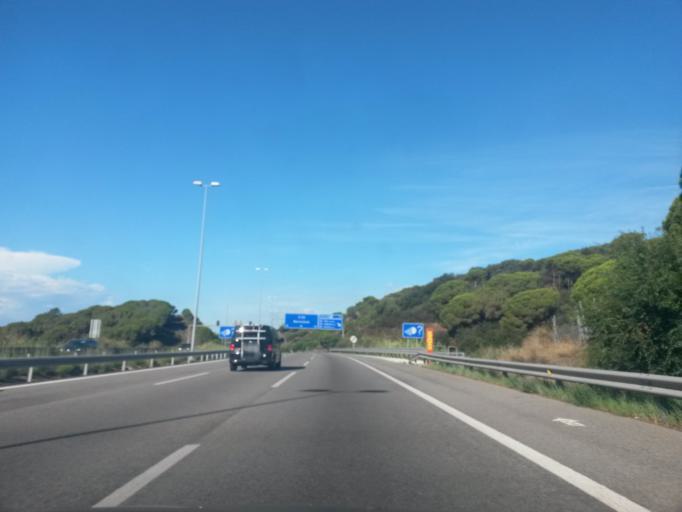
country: ES
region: Catalonia
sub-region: Provincia de Barcelona
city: Sant Pol de Mar
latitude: 41.6106
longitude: 2.6242
